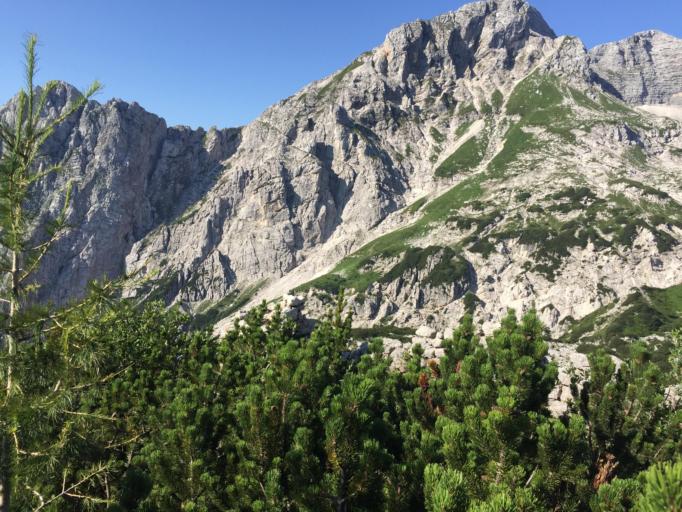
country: SI
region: Bovec
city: Bovec
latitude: 46.3866
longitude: 13.5306
